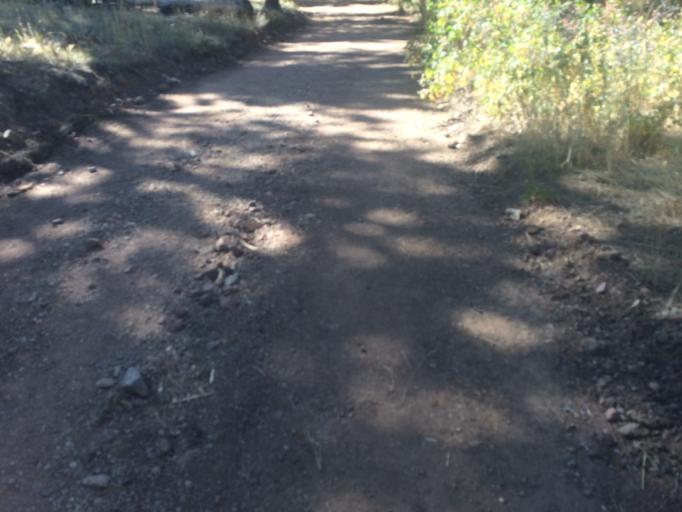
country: US
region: Colorado
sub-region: Boulder County
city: Boulder
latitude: 39.9656
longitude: -105.2731
